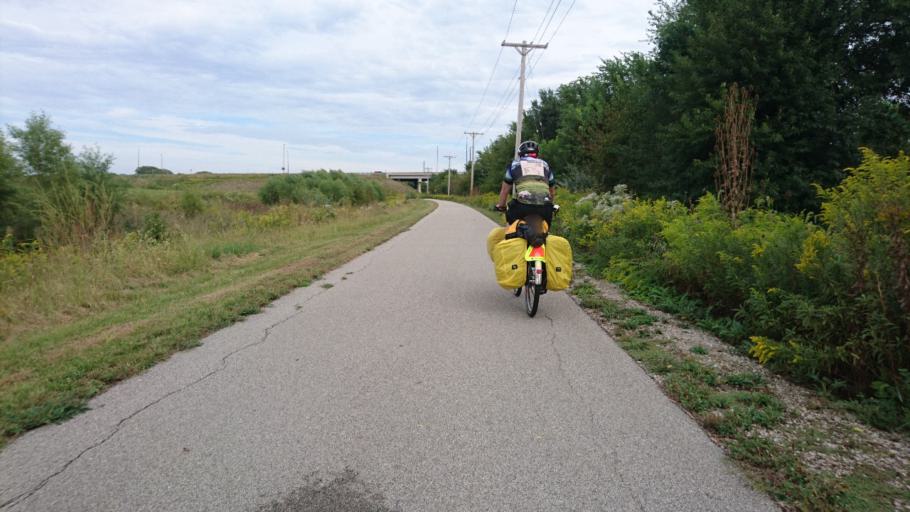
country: US
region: Illinois
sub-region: Sangamon County
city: Southern View
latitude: 39.7429
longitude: -89.6745
